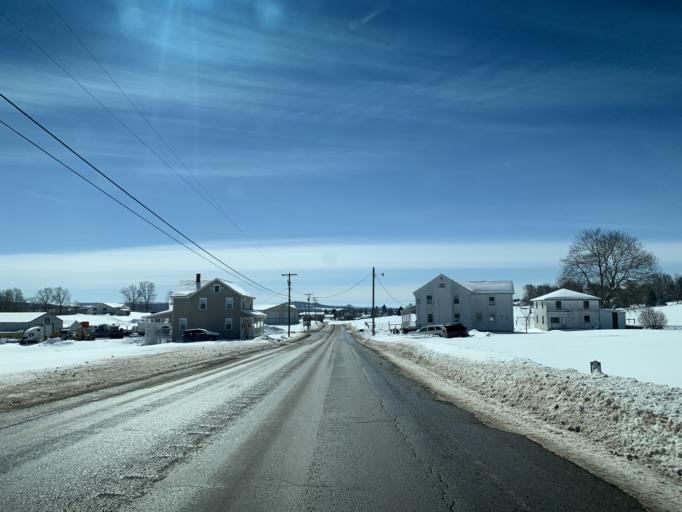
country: US
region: Pennsylvania
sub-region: Somerset County
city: Meyersdale
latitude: 39.7101
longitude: -79.1607
